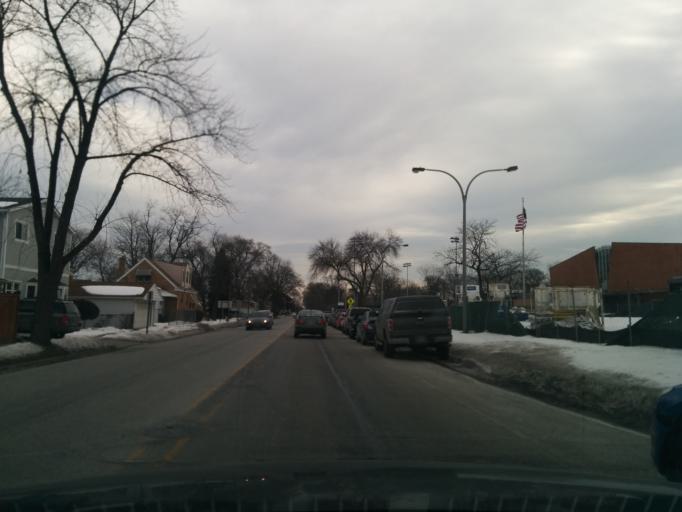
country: US
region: Illinois
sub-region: Cook County
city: River Grove
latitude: 41.9230
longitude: -87.8306
